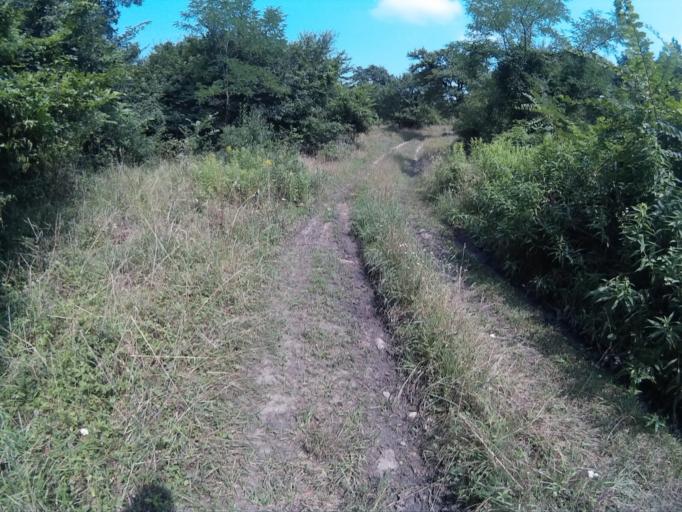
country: HU
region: Veszprem
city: Papa
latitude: 47.2956
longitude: 17.6190
